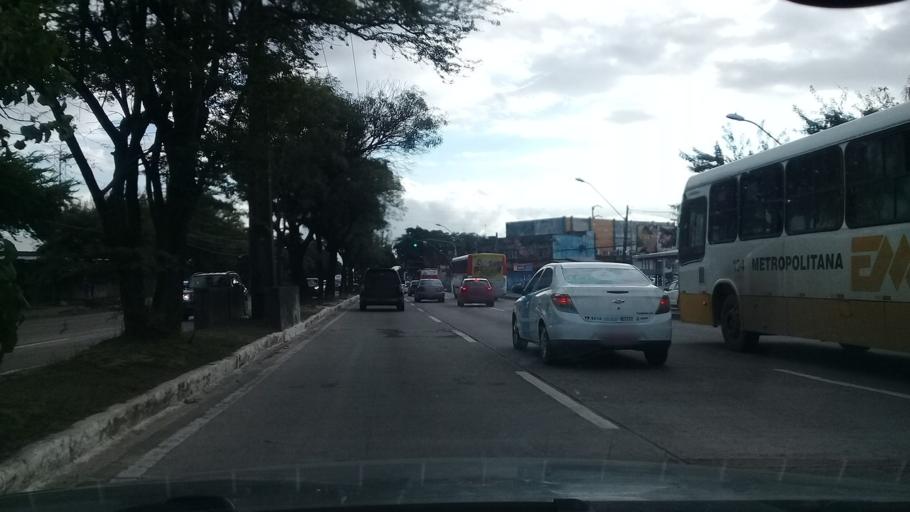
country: BR
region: Pernambuco
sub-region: Recife
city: Recife
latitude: -8.0613
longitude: -34.9293
